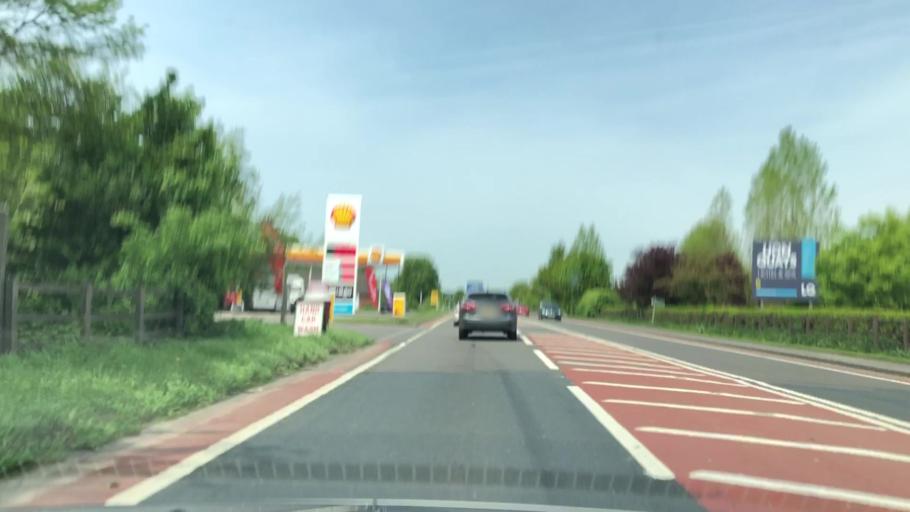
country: GB
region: England
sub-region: Shropshire
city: Gobowen
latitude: 52.9130
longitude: -3.0424
